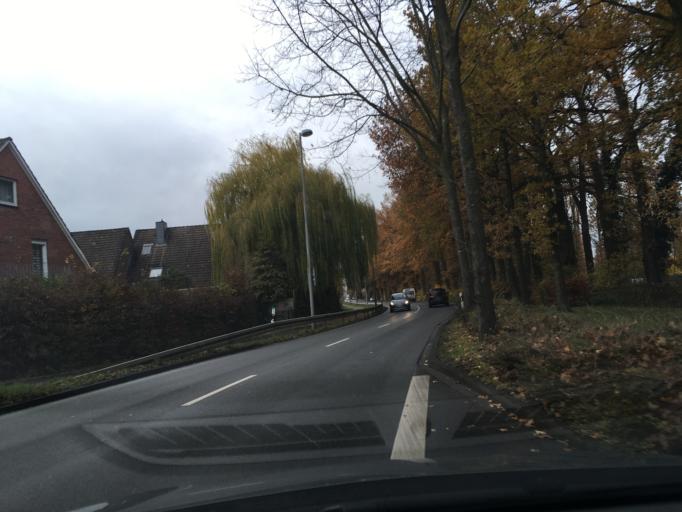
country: DE
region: North Rhine-Westphalia
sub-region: Regierungsbezirk Munster
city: Ahaus
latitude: 52.0855
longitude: 6.9991
